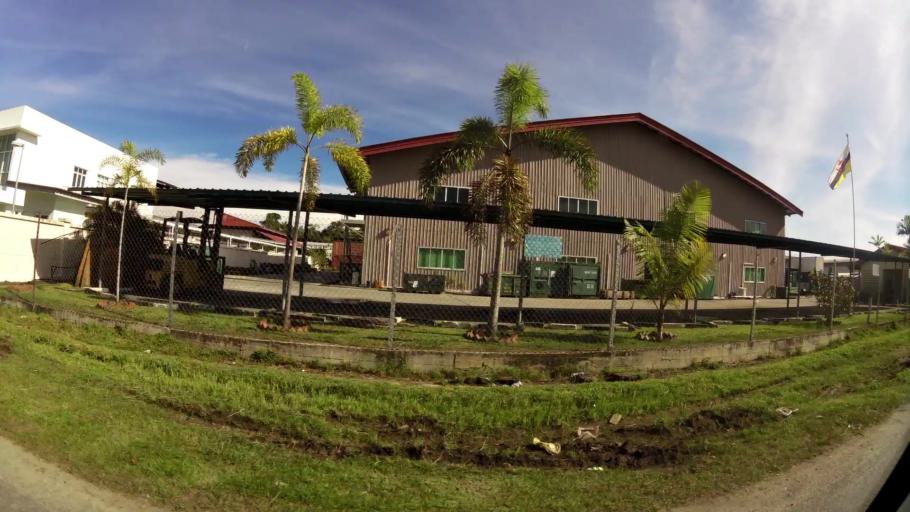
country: BN
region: Belait
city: Kuala Belait
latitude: 4.5728
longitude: 114.2063
